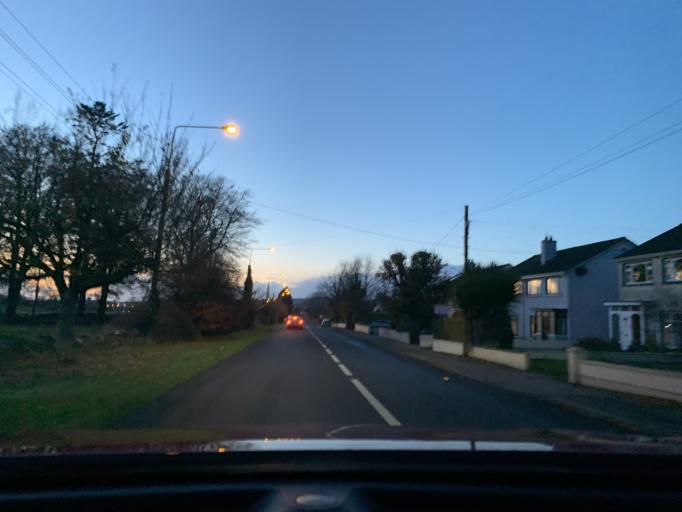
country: IE
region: Connaught
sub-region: Roscommon
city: Boyle
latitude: 53.9704
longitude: -8.2825
